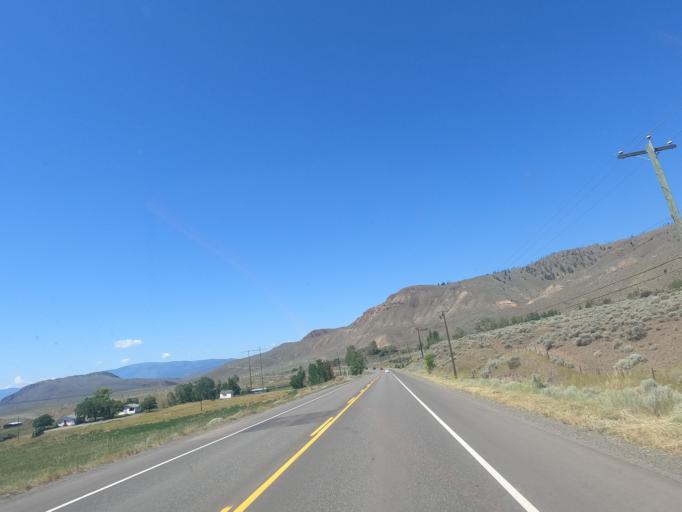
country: CA
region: British Columbia
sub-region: Thompson-Nicola Regional District
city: Ashcroft
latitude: 50.7978
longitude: -121.1235
